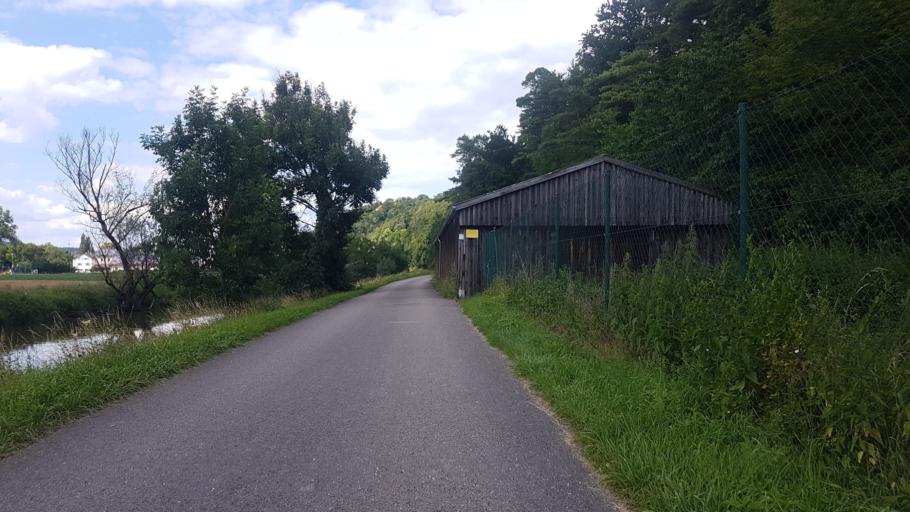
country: DE
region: Bavaria
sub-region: Regierungsbezirk Mittelfranken
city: Treuchtlingen
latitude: 48.9385
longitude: 10.9320
